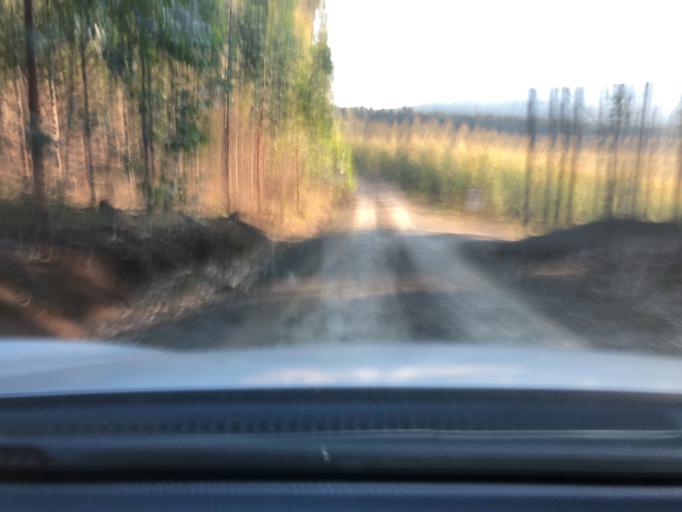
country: ZA
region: KwaZulu-Natal
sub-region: Sisonke District Municipality
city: Ixopo
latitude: -30.1835
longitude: 30.0537
